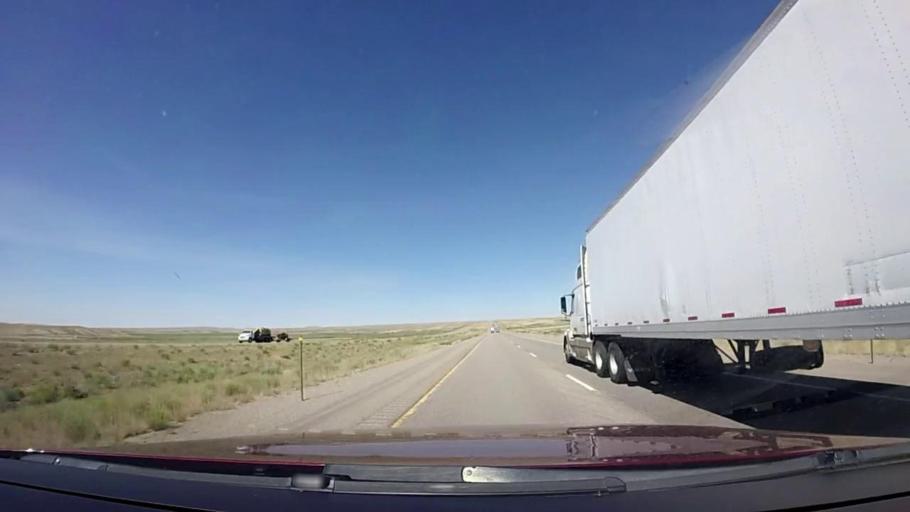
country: US
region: Wyoming
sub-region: Sweetwater County
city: Rock Springs
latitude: 41.6407
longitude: -108.4948
